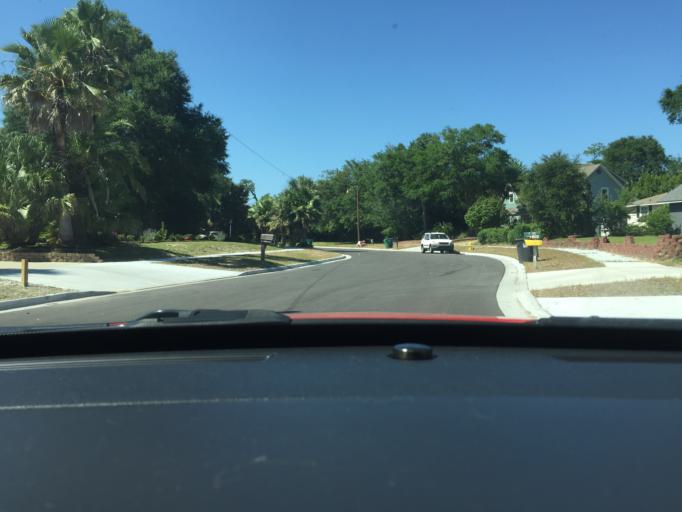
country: US
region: Mississippi
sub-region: Harrison County
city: Biloxi
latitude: 30.3931
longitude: -88.9852
